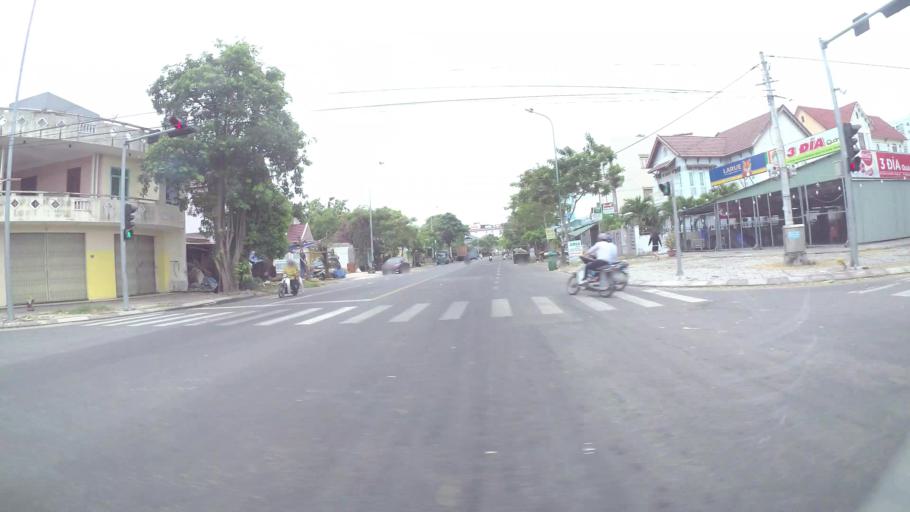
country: VN
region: Da Nang
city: Da Nang
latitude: 16.0900
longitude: 108.2355
